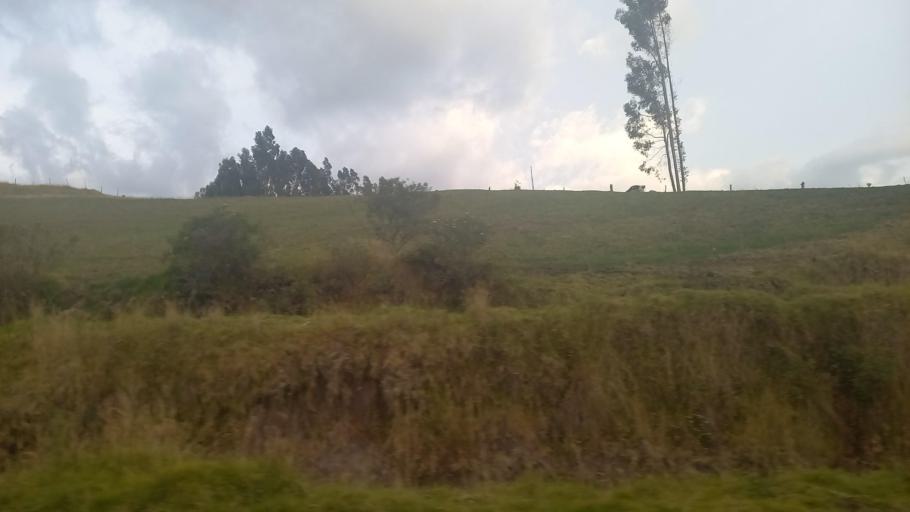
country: EC
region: Pichincha
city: Cayambe
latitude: 0.0864
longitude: -78.1021
